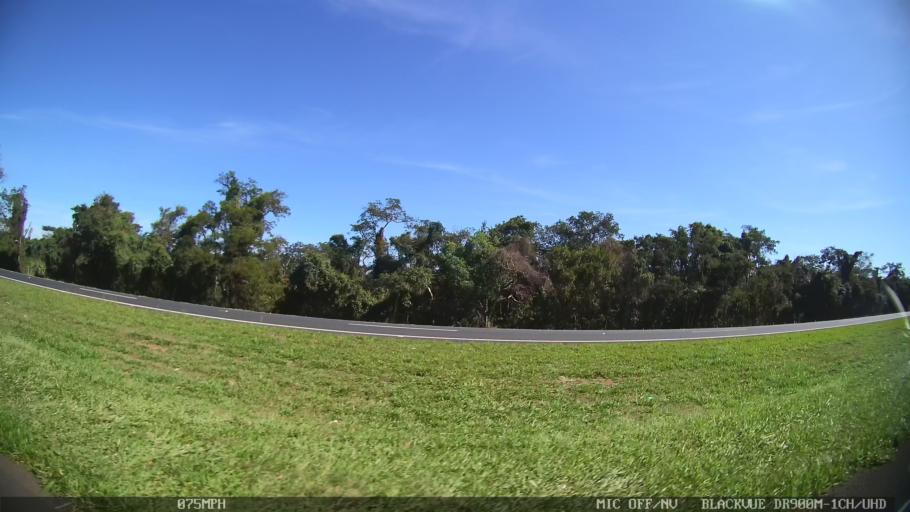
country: BR
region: Sao Paulo
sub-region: Santa Rita Do Passa Quatro
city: Santa Rita do Passa Quatro
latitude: -21.6370
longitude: -47.6125
